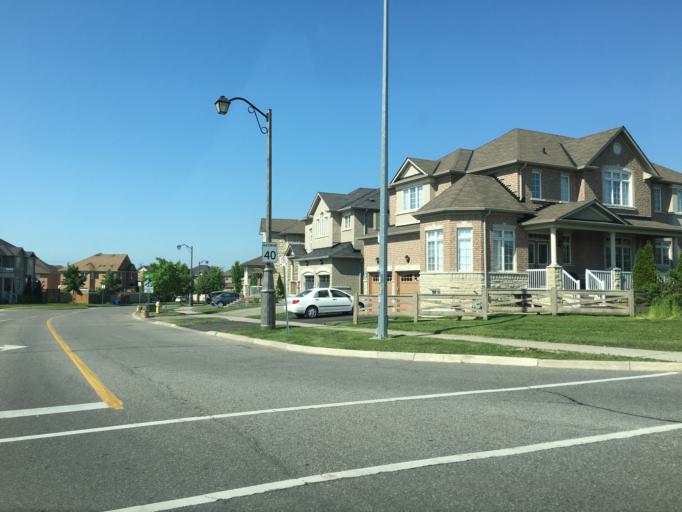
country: CA
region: Ontario
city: Markham
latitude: 43.8580
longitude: -79.2217
